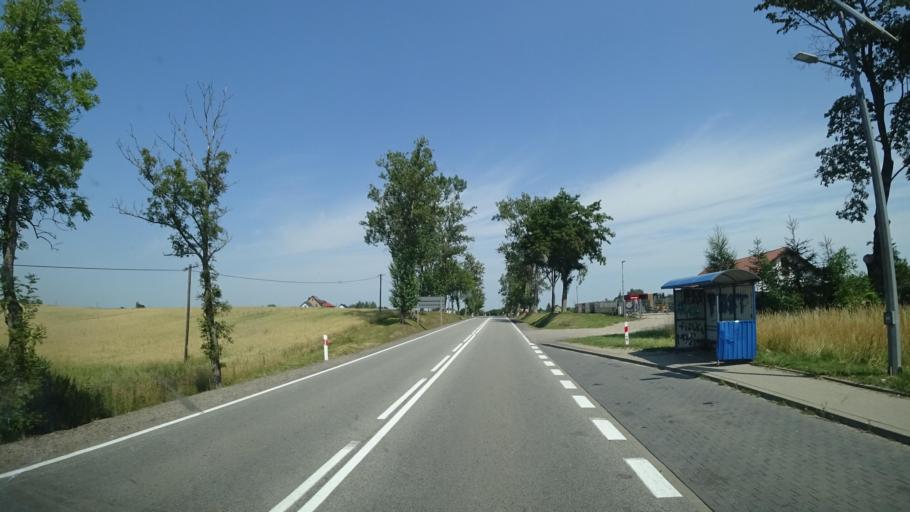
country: PL
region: Pomeranian Voivodeship
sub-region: Powiat koscierski
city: Koscierzyna
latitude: 54.1412
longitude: 18.0200
